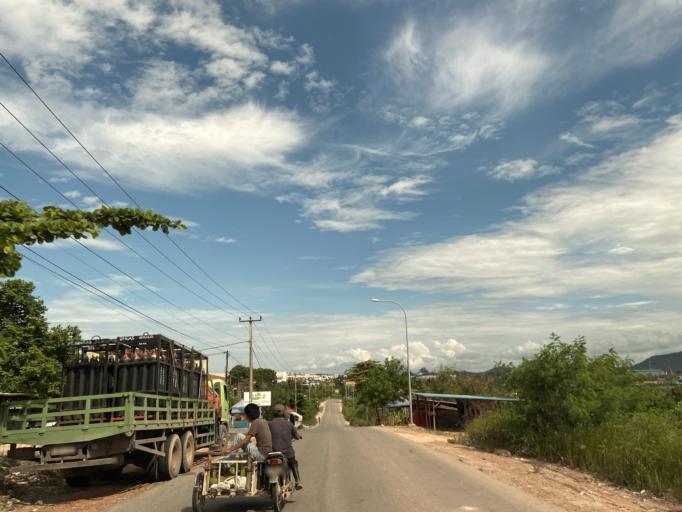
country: SG
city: Singapore
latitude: 1.0256
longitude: 103.9448
